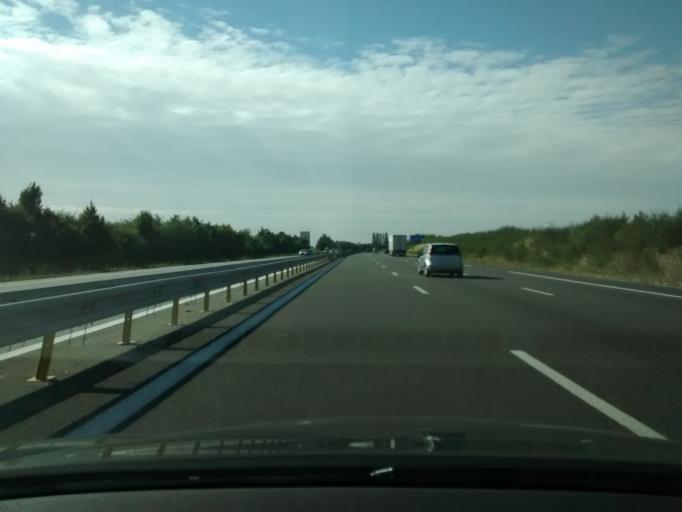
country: FR
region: Ile-de-France
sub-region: Departement des Yvelines
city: Saint-Arnoult-en-Yvelines
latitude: 48.5316
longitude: 1.9053
